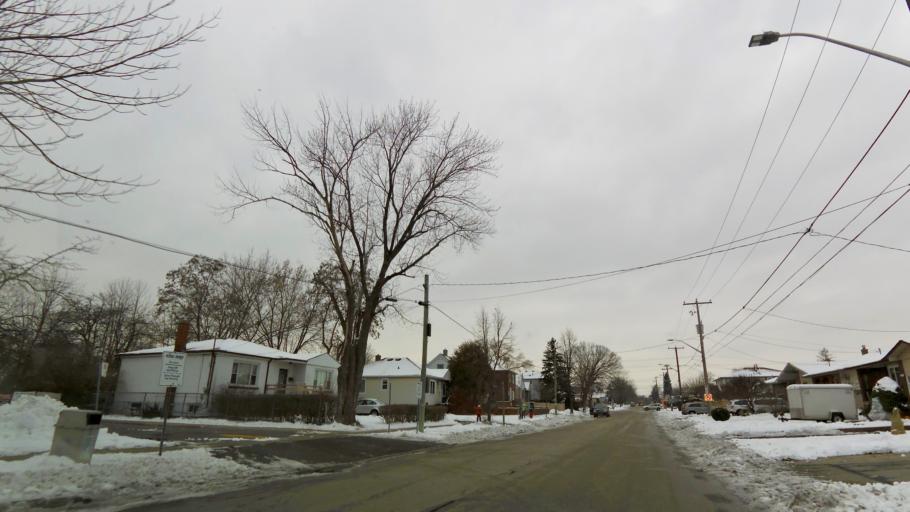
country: CA
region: Ontario
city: Etobicoke
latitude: 43.5788
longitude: -79.5665
